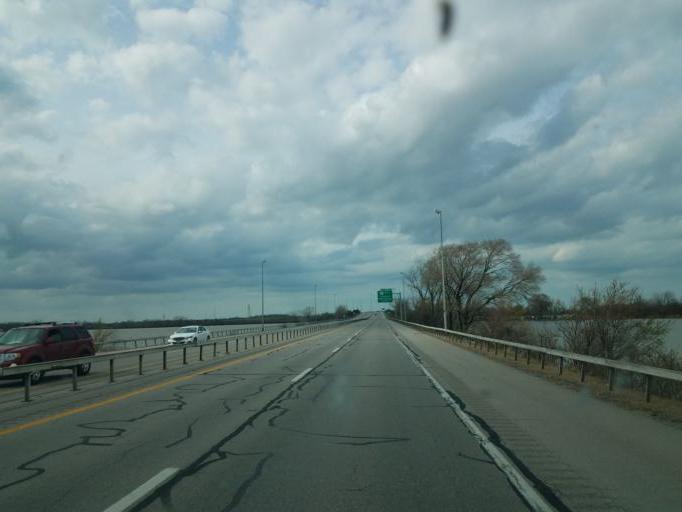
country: US
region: Ohio
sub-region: Ottawa County
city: Port Clinton
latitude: 41.4928
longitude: -82.8359
